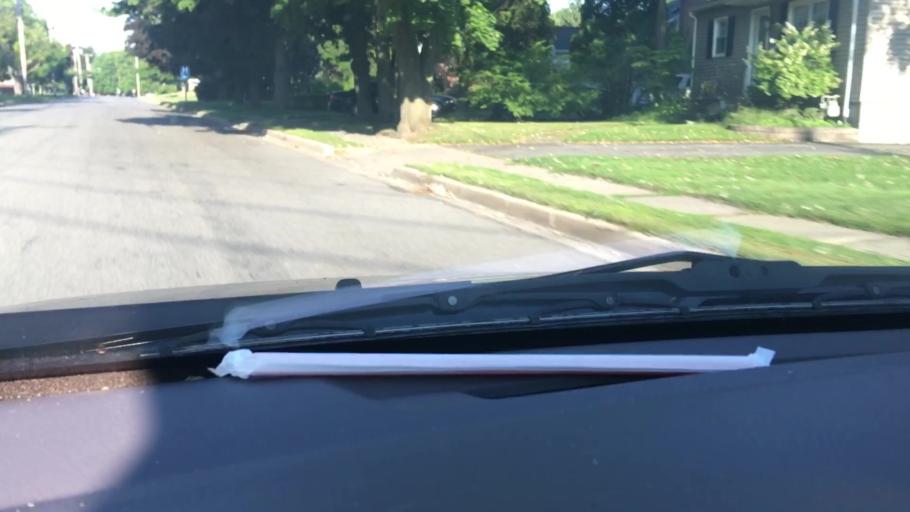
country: US
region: New York
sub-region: Genesee County
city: Batavia
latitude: 43.0090
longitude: -78.1735
